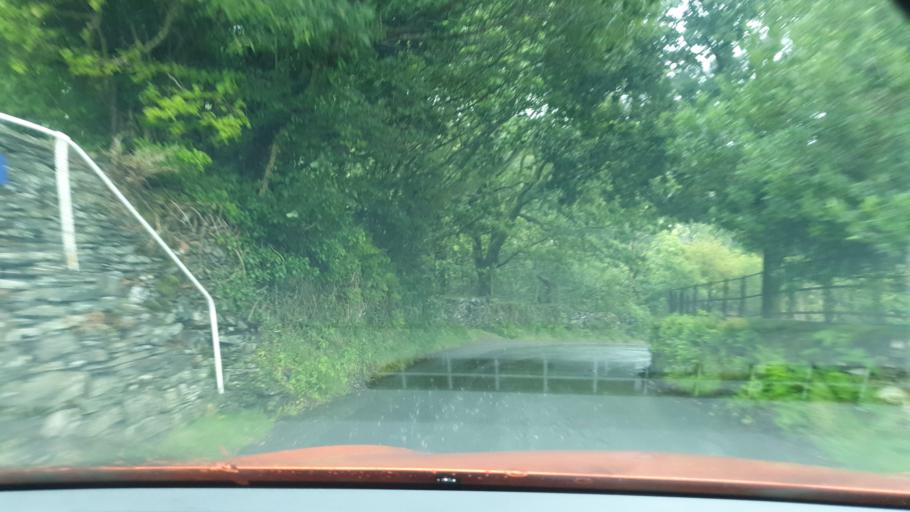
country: GB
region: England
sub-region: Cumbria
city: Millom
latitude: 54.3284
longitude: -3.2350
